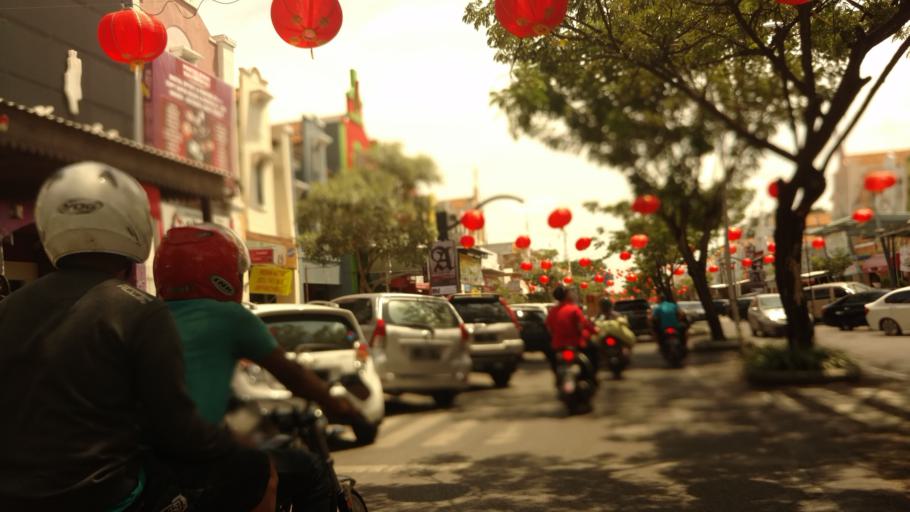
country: ID
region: East Java
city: Driyorejo
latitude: -7.2862
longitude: 112.6560
